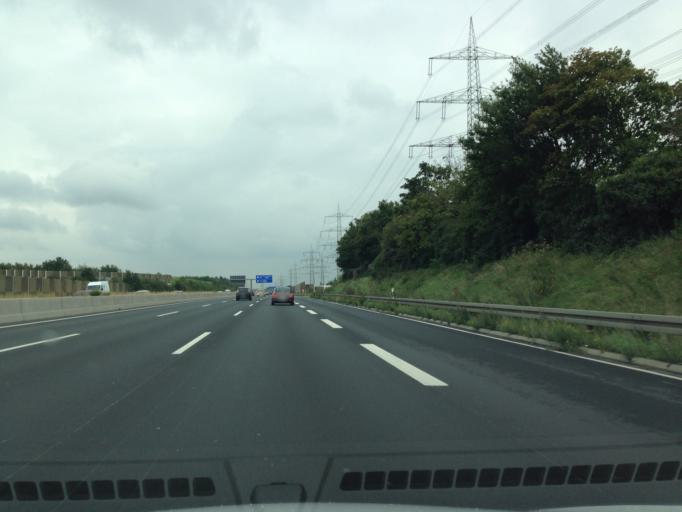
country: DE
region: North Rhine-Westphalia
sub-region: Regierungsbezirk Dusseldorf
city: Kaarst
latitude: 51.2089
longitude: 6.6479
